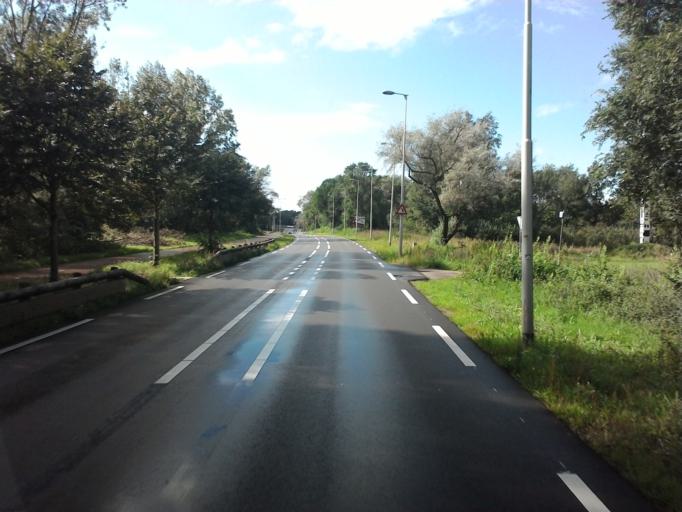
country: NL
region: North Holland
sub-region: Gemeente Beverwijk
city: Beverwijk
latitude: 52.4901
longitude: 4.6122
